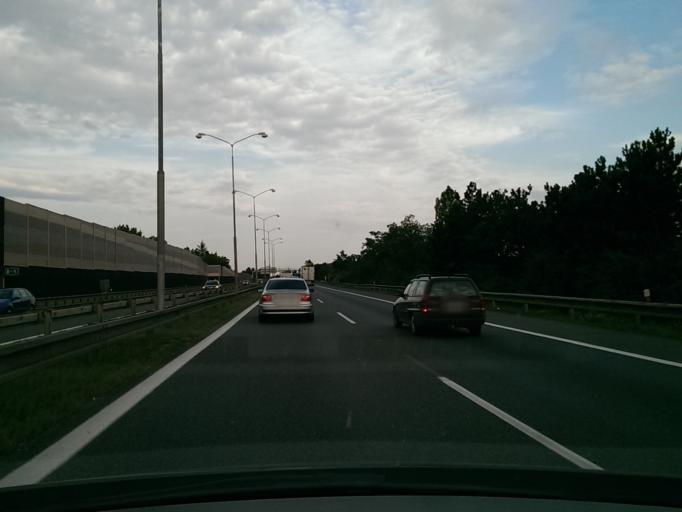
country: CZ
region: South Moravian
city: Ostopovice
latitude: 49.1650
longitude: 16.5528
